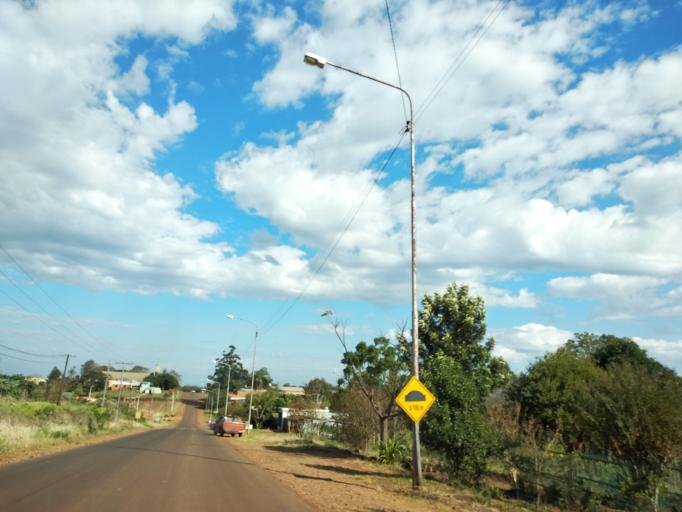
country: AR
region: Misiones
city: Aristobulo del Valle
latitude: -27.0802
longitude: -54.8315
